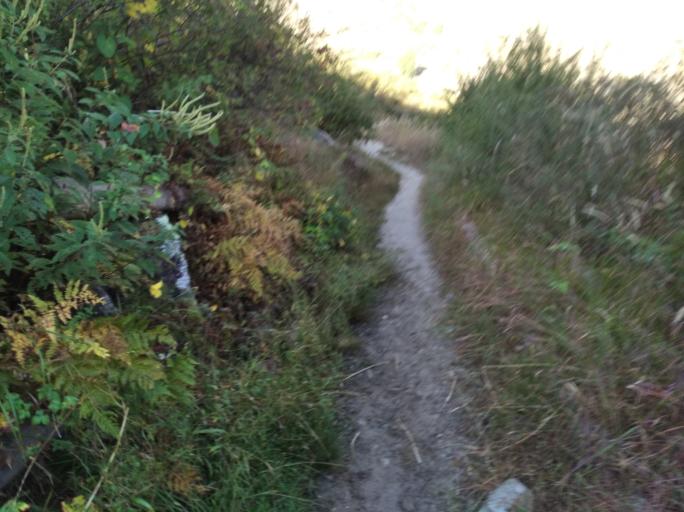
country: NP
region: Western Region
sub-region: Dhawalagiri Zone
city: Jomsom
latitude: 28.8814
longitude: 82.9764
